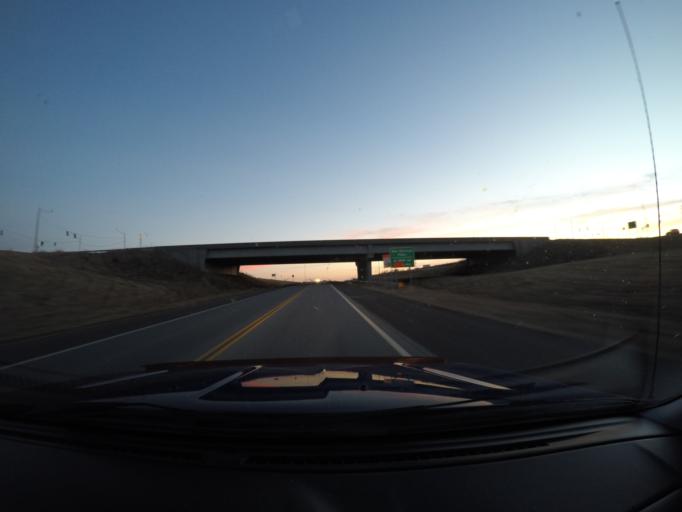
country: US
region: Kansas
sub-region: Douglas County
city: Lawrence
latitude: 38.9722
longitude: -95.3343
